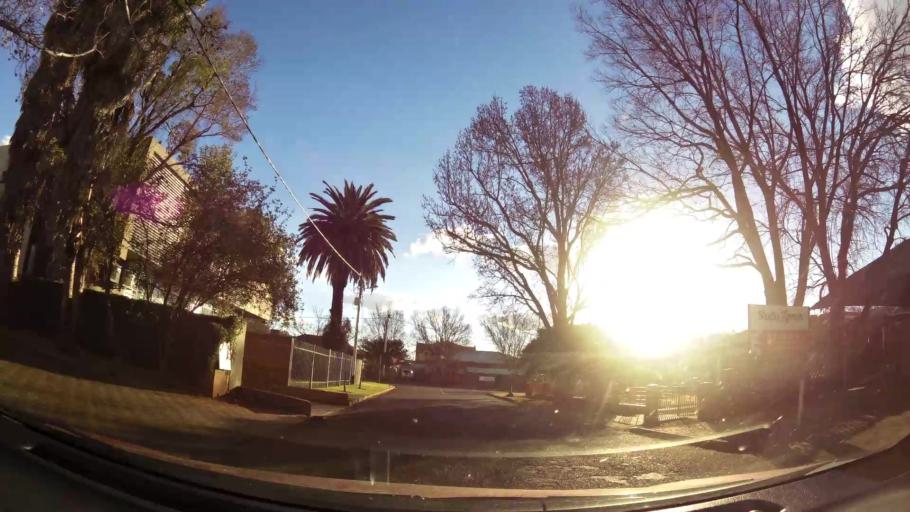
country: ZA
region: North-West
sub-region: Dr Kenneth Kaunda District Municipality
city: Potchefstroom
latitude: -26.7084
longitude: 27.1000
